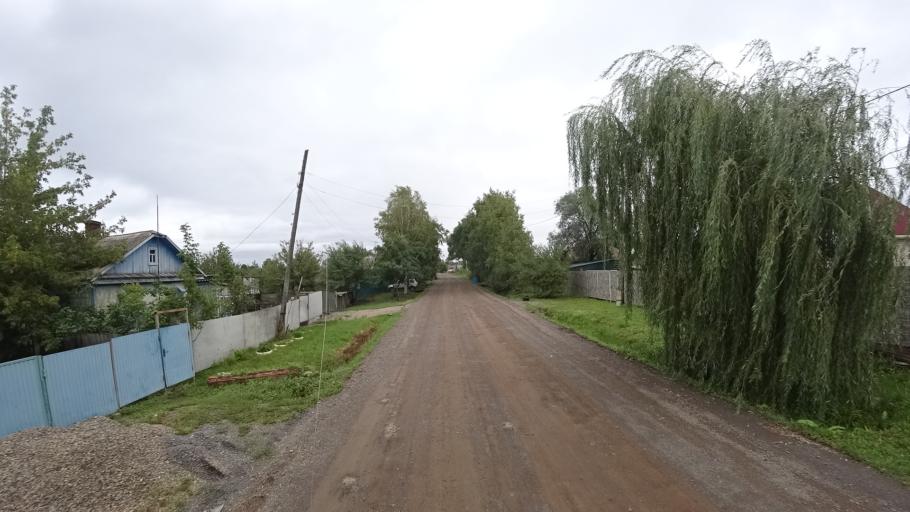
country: RU
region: Primorskiy
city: Chernigovka
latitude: 44.3484
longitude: 132.5721
